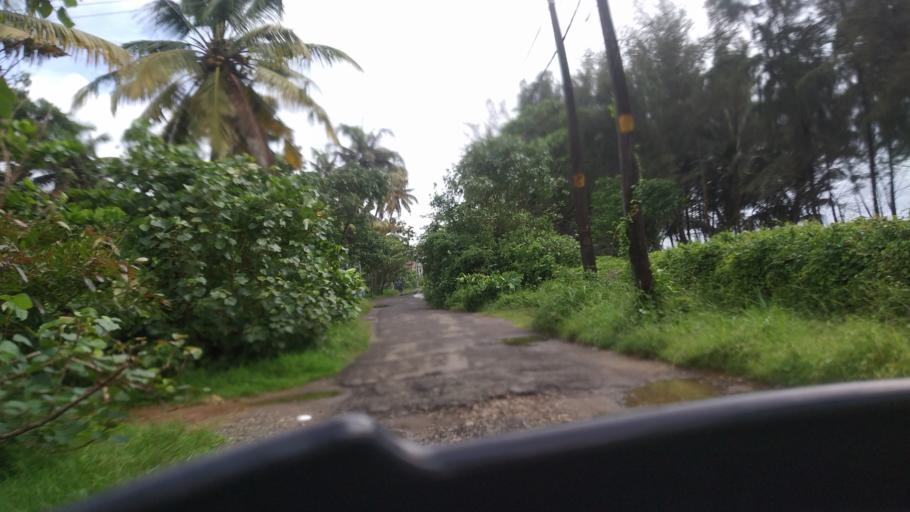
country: IN
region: Kerala
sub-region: Ernakulam
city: Elur
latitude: 10.1063
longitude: 76.1884
